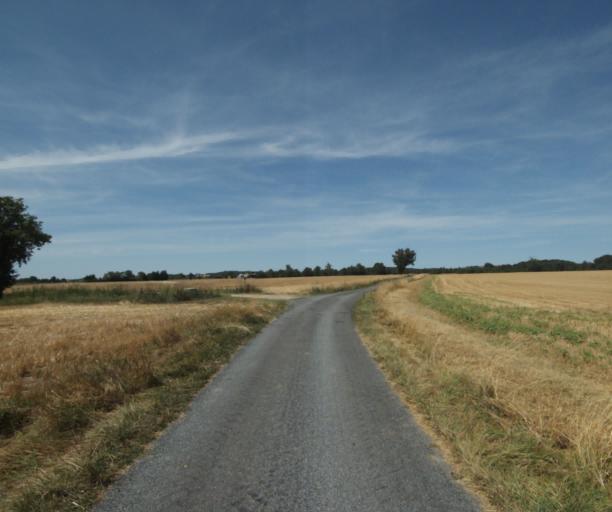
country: FR
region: Midi-Pyrenees
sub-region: Departement du Tarn
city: Puylaurens
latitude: 43.5293
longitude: 2.0030
